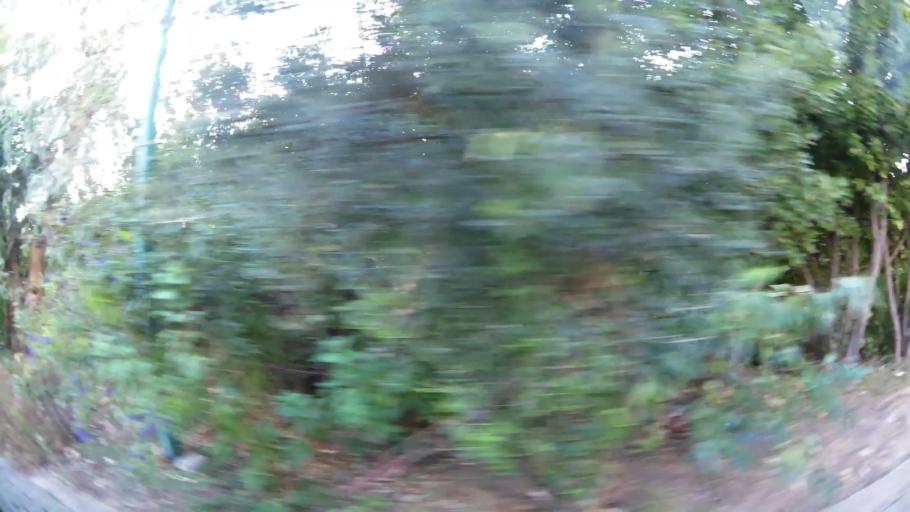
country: GR
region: Attica
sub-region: Nomarchia Anatolikis Attikis
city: Kryoneri
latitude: 38.1374
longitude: 23.8292
